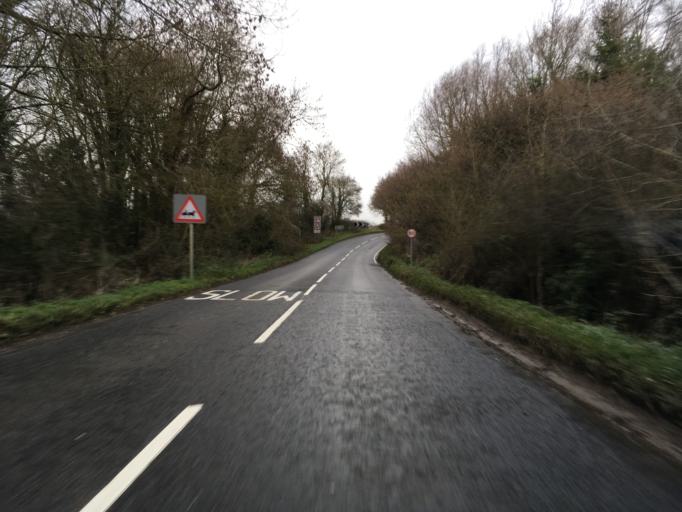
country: GB
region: England
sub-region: Wiltshire
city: Malmesbury
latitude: 51.6151
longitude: -2.1230
